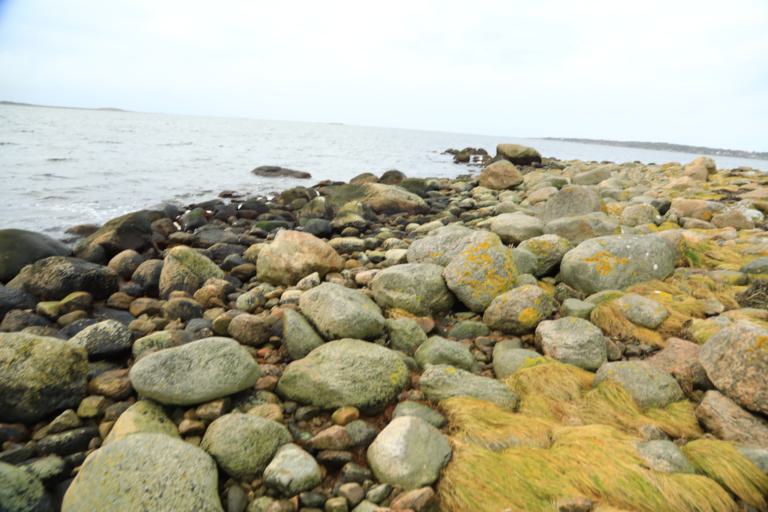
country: SE
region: Halland
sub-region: Varbergs Kommun
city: Varberg
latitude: 57.1775
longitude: 12.2026
